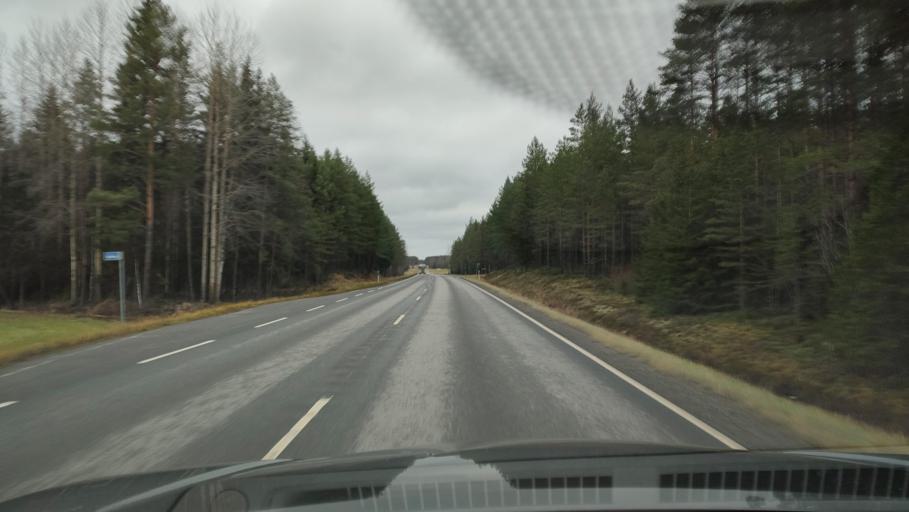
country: FI
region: Southern Ostrobothnia
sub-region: Suupohja
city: Kauhajoki
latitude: 62.4934
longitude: 22.2966
